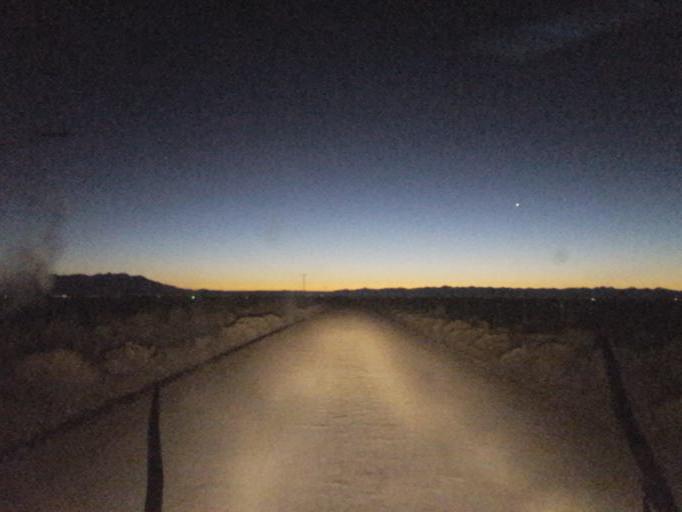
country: US
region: Colorado
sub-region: Rio Grande County
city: Monte Vista
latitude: 37.4011
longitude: -106.1090
